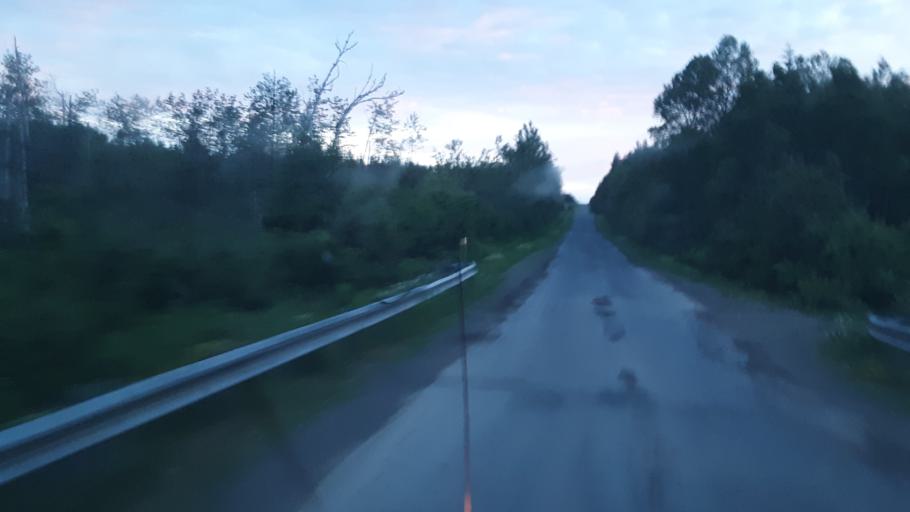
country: US
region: Maine
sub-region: Aroostook County
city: Caribou
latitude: 46.8539
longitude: -68.0920
